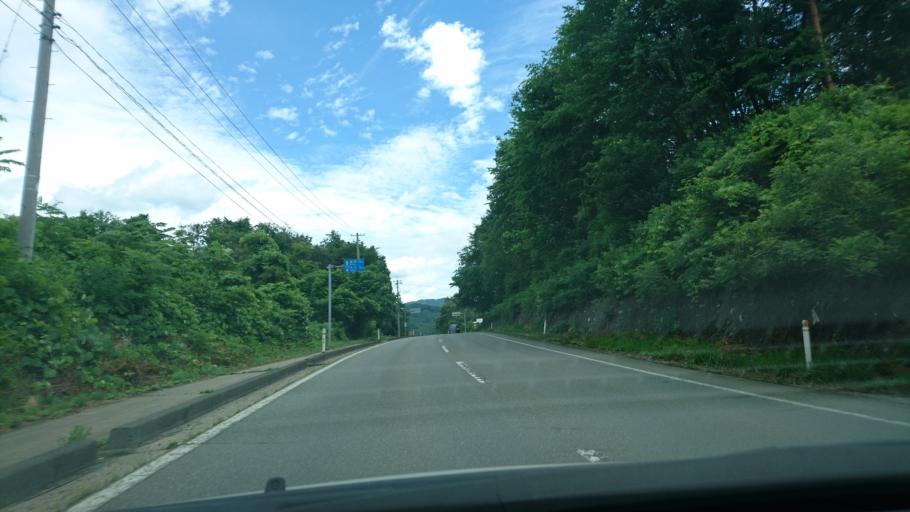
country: JP
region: Iwate
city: Morioka-shi
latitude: 39.6009
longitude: 141.2033
